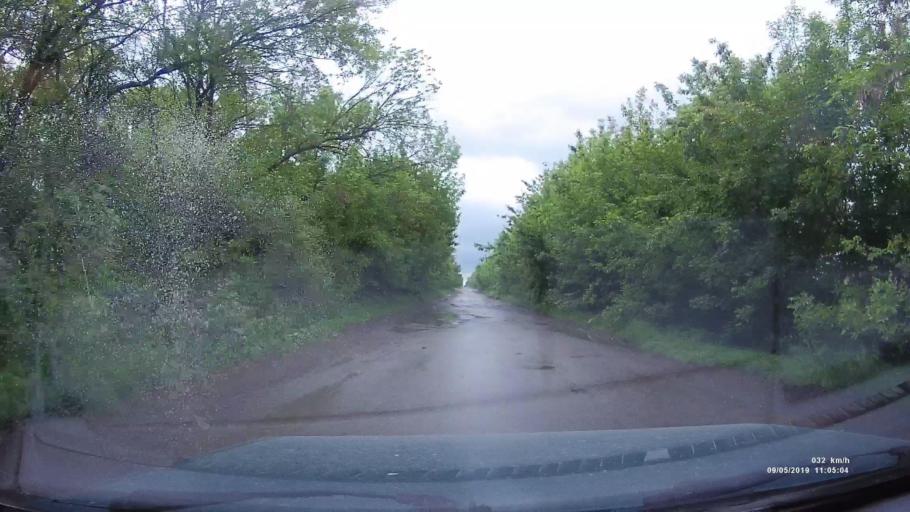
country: RU
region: Krasnodarskiy
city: Kanelovskaya
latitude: 46.8116
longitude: 39.2099
